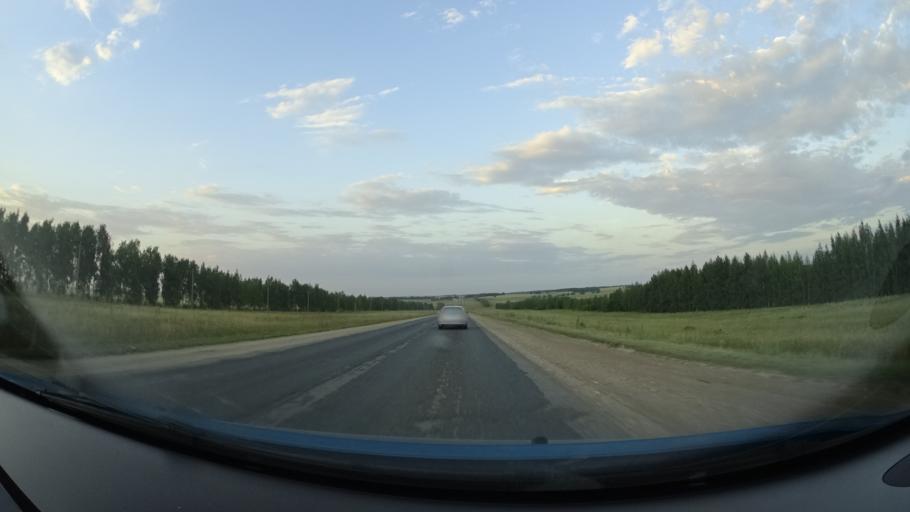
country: RU
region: Orenburg
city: Severnoye
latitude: 54.2284
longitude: 52.7595
